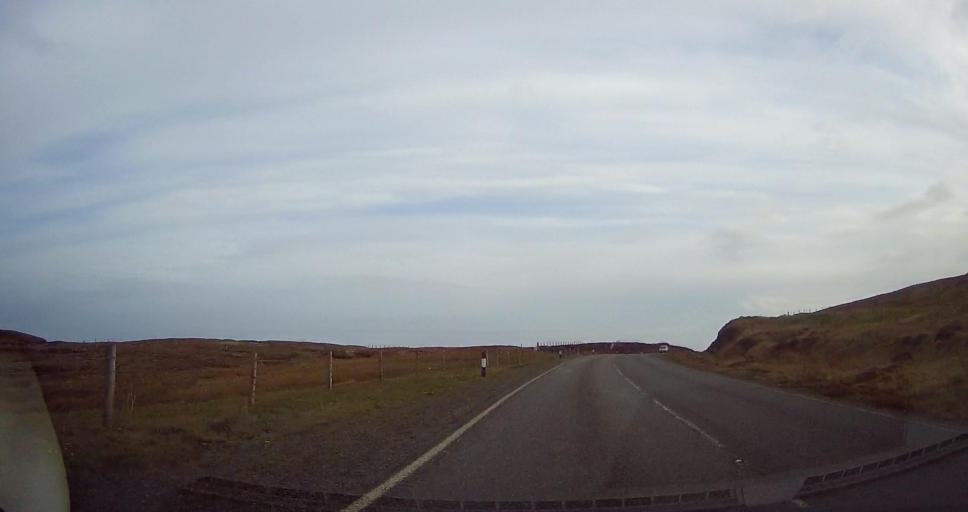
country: GB
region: Scotland
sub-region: Shetland Islands
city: Sandwick
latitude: 60.0910
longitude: -1.2282
